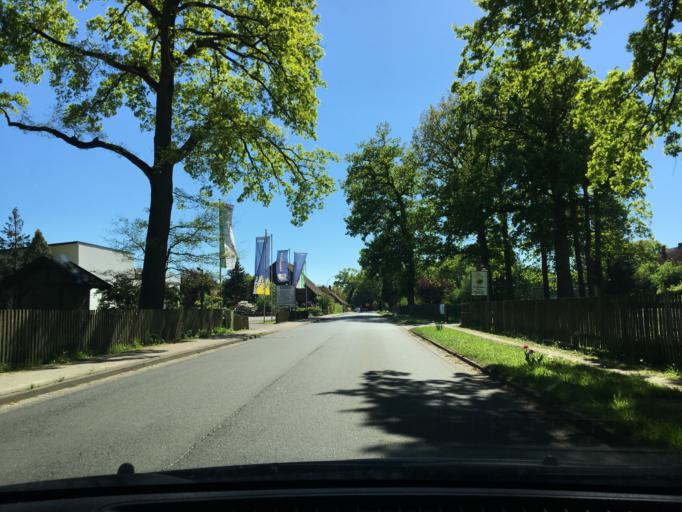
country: DE
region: Lower Saxony
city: Hermannsburg
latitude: 52.8480
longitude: 10.0802
